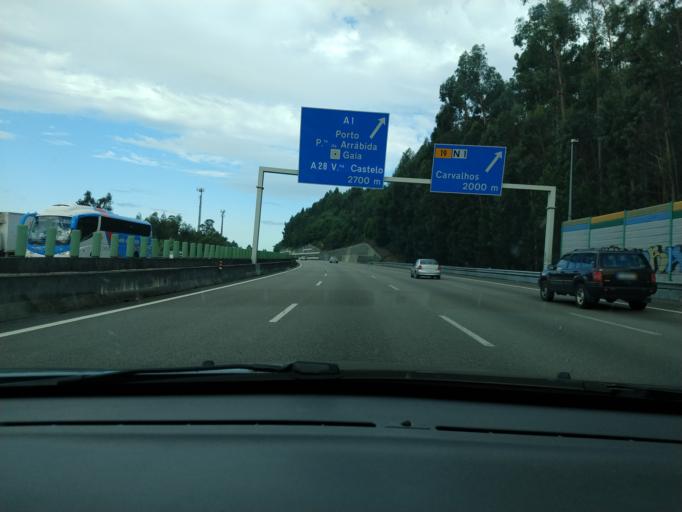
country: PT
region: Porto
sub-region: Vila Nova de Gaia
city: Perozinho
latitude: 41.0513
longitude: -8.5724
